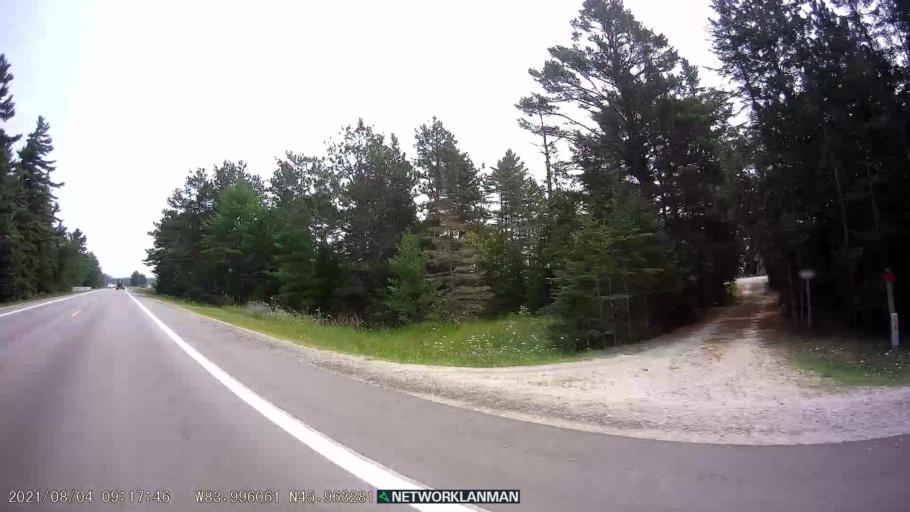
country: CA
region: Ontario
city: Thessalon
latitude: 45.9641
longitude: -83.9941
